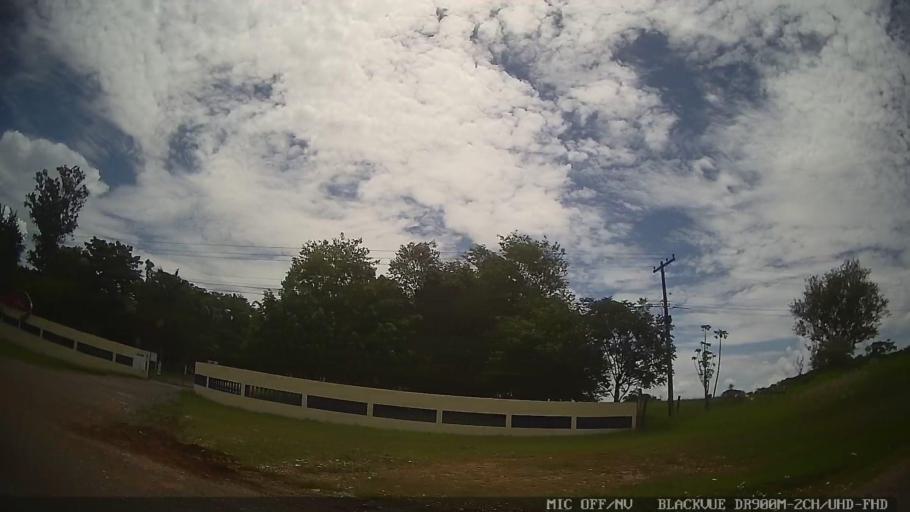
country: BR
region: Sao Paulo
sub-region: Conchas
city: Conchas
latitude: -23.0527
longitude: -47.9593
